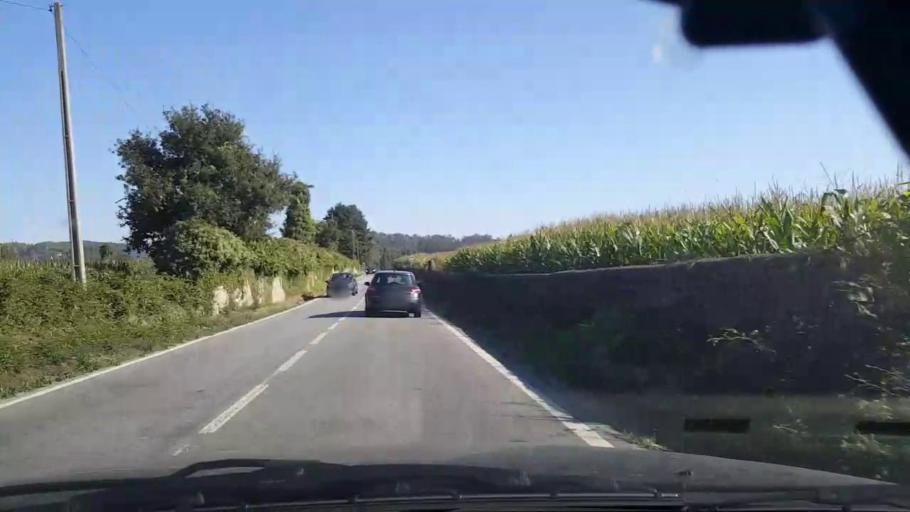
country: PT
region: Porto
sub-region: Vila do Conde
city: Arvore
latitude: 41.3298
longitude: -8.6611
